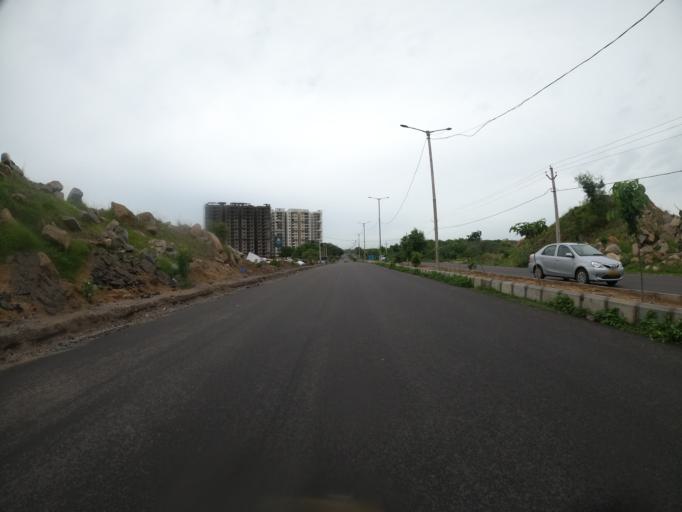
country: IN
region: Telangana
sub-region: Rangareddi
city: Kukatpalli
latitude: 17.4621
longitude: 78.3890
